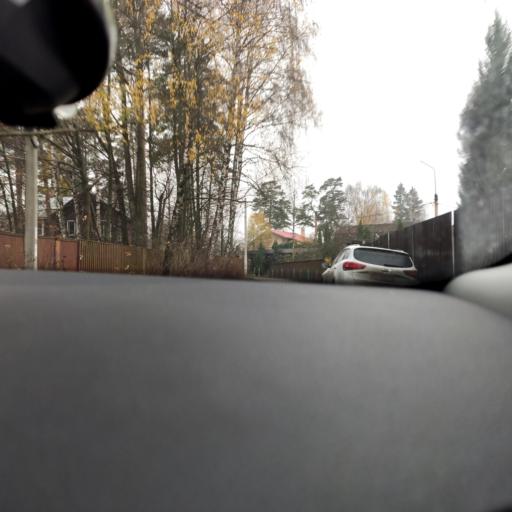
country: RU
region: Moskovskaya
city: Nakhabino
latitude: 55.8515
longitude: 37.1603
